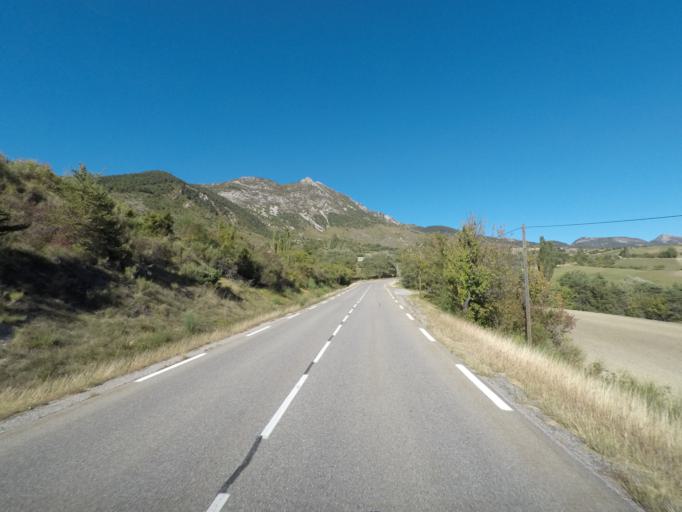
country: FR
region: Provence-Alpes-Cote d'Azur
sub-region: Departement des Hautes-Alpes
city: Serres
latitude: 44.4083
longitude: 5.5330
